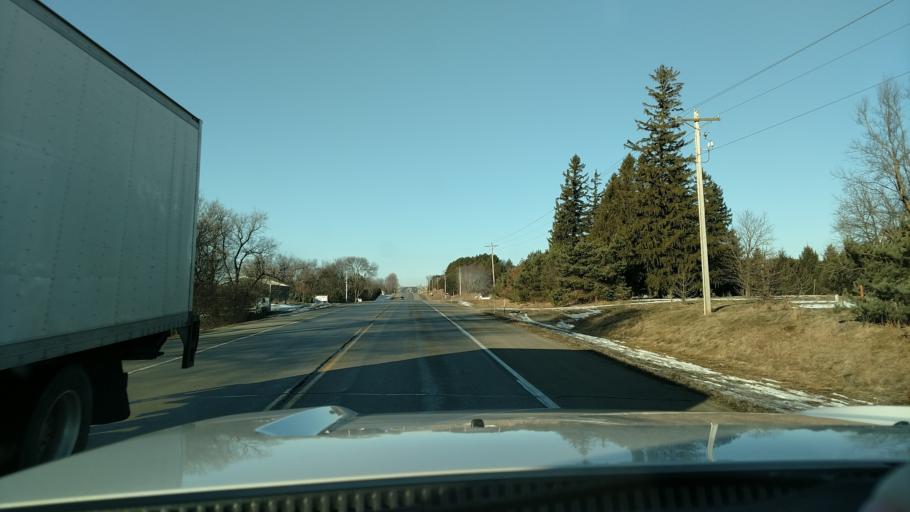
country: US
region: Minnesota
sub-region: Olmsted County
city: Oronoco
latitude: 44.1082
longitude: -92.4952
